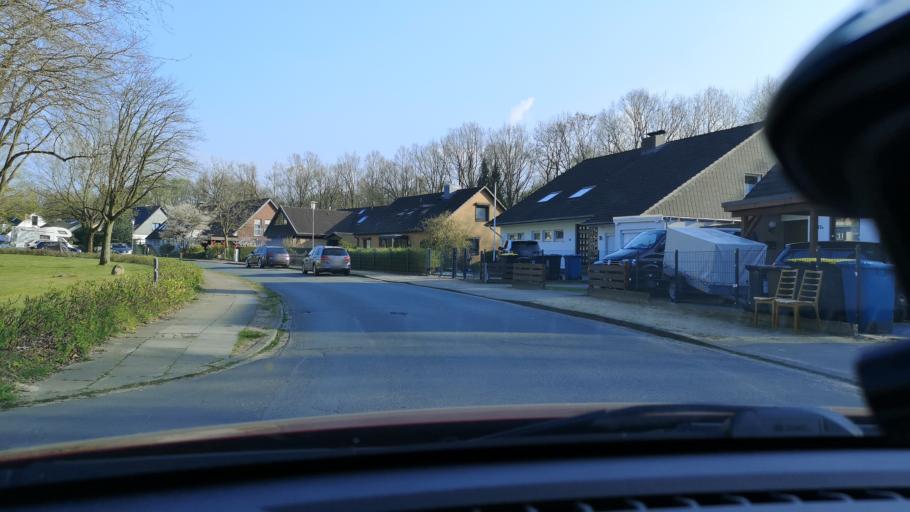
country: DE
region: Schleswig-Holstein
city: Ahrensburg
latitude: 53.6696
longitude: 10.2089
